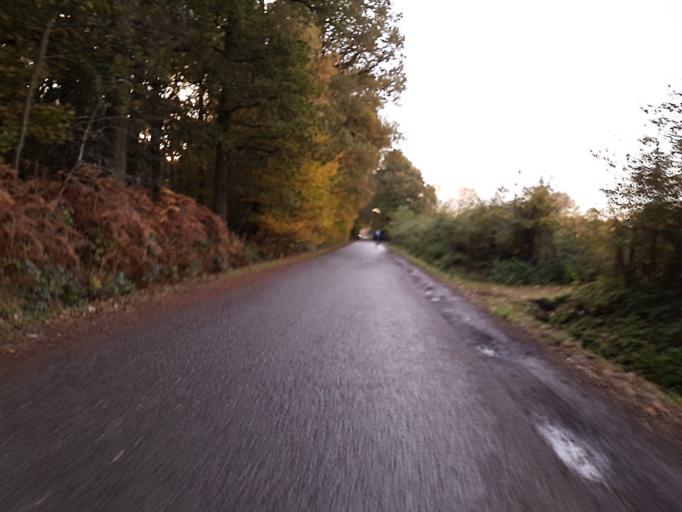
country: BE
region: Flanders
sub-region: Provincie Antwerpen
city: Ranst
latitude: 51.2015
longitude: 4.5569
